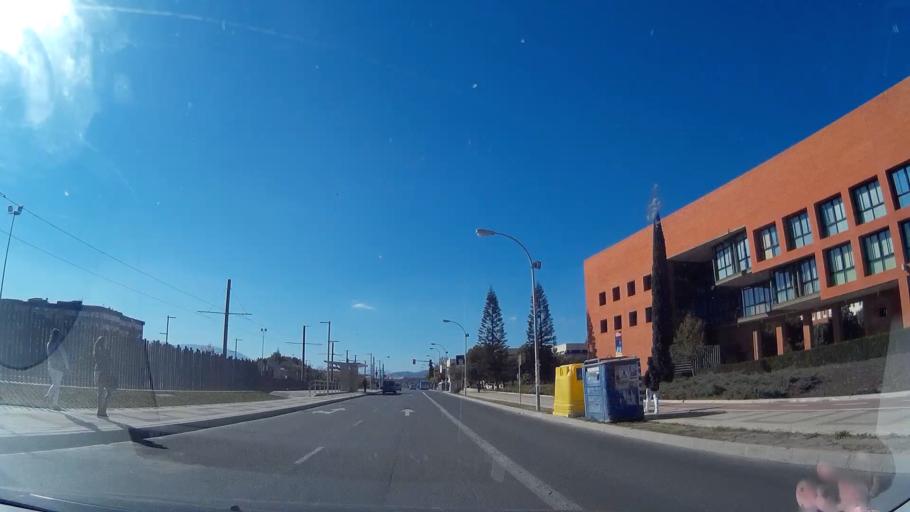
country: ES
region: Andalusia
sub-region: Provincia de Malaga
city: Malaga
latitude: 36.7173
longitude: -4.4715
